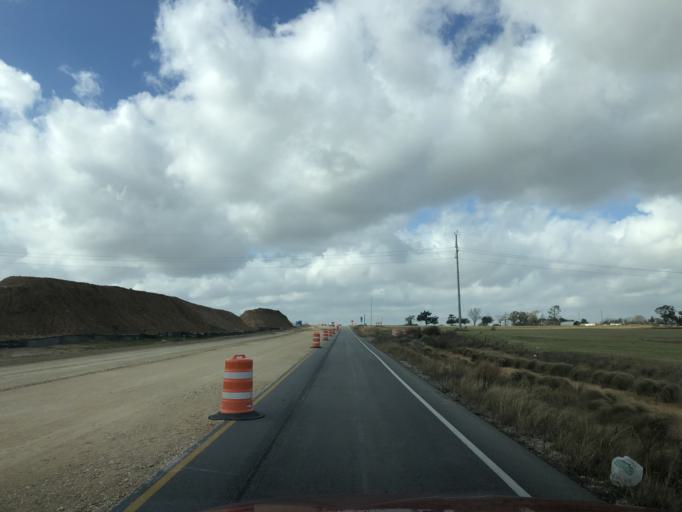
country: US
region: Texas
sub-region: Austin County
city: Sealy
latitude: 29.7623
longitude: -96.1618
